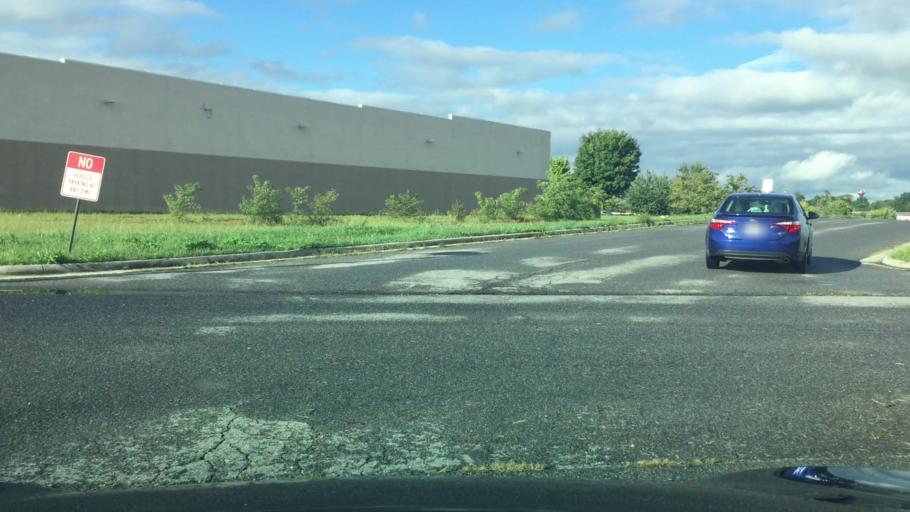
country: US
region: Virginia
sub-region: Wythe County
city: Wytheville
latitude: 36.9560
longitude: -81.1027
